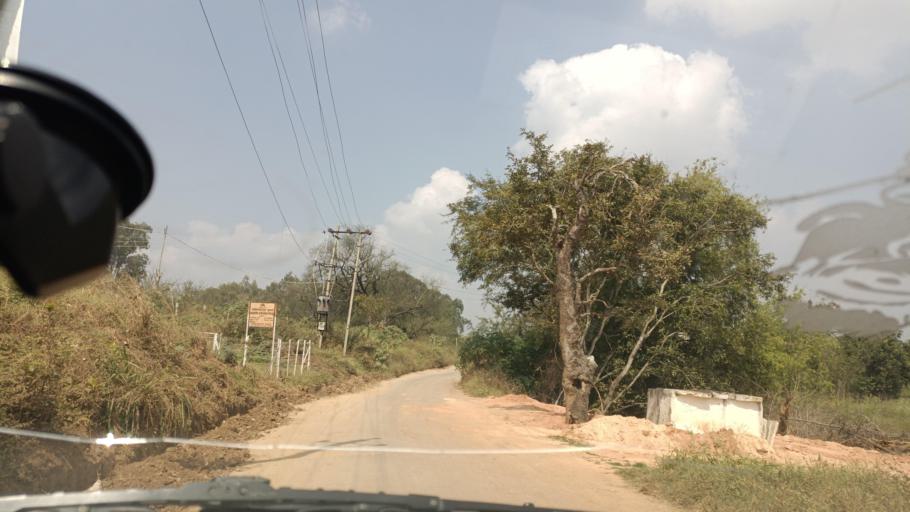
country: IN
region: Karnataka
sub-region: Bangalore Urban
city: Yelahanka
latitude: 13.1754
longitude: 77.6313
